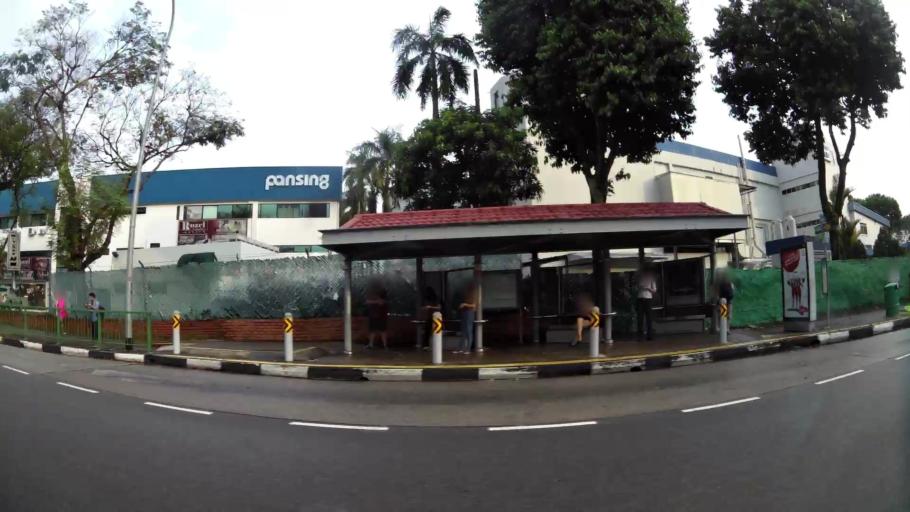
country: SG
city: Singapore
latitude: 1.3593
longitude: 103.8552
